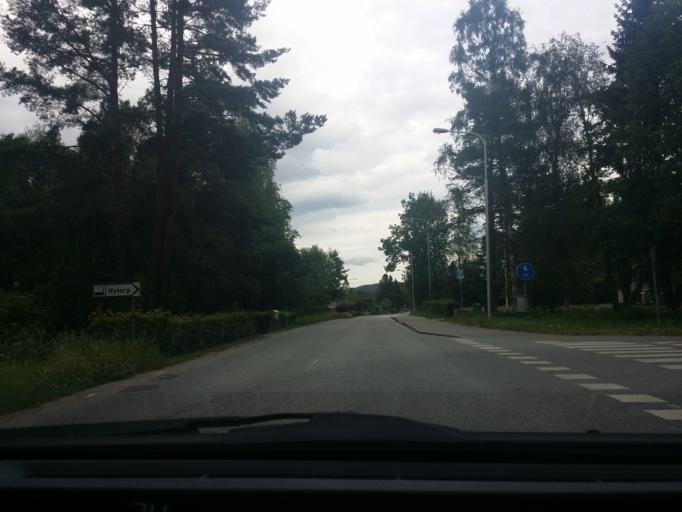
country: SE
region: OErebro
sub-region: Nora Kommun
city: Nora
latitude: 59.5305
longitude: 15.0341
